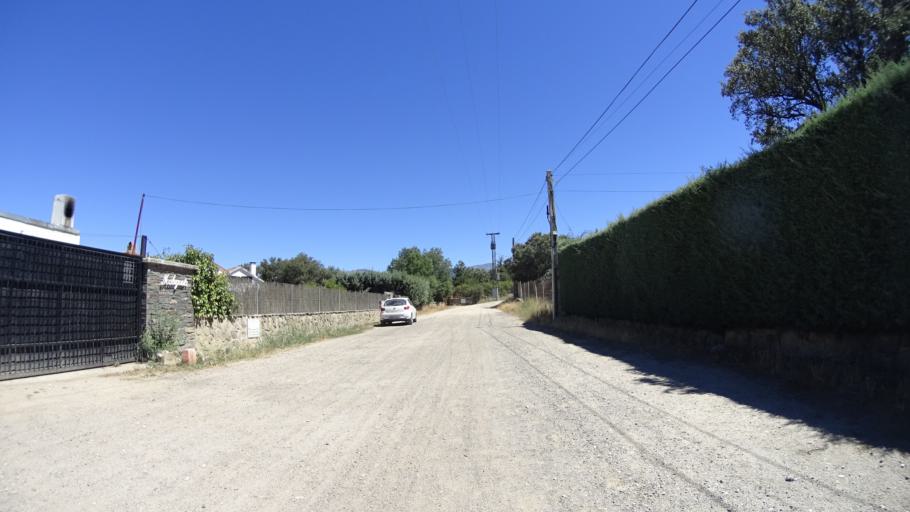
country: ES
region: Madrid
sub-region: Provincia de Madrid
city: Alpedrete
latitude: 40.6678
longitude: -4.0474
